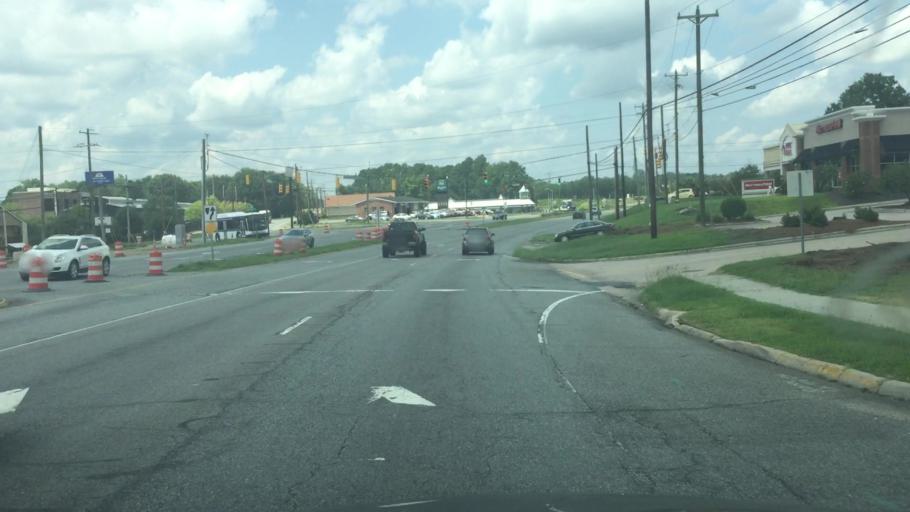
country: US
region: North Carolina
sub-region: Cabarrus County
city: Concord
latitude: 35.4409
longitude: -80.6076
